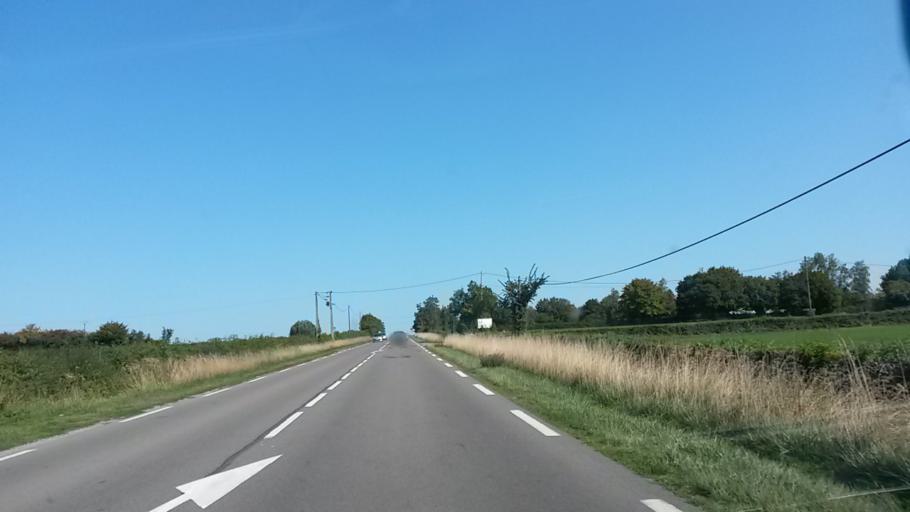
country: FR
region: Nord-Pas-de-Calais
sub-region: Departement du Nord
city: Avesnes-sur-Helpe
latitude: 50.1018
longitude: 3.9311
